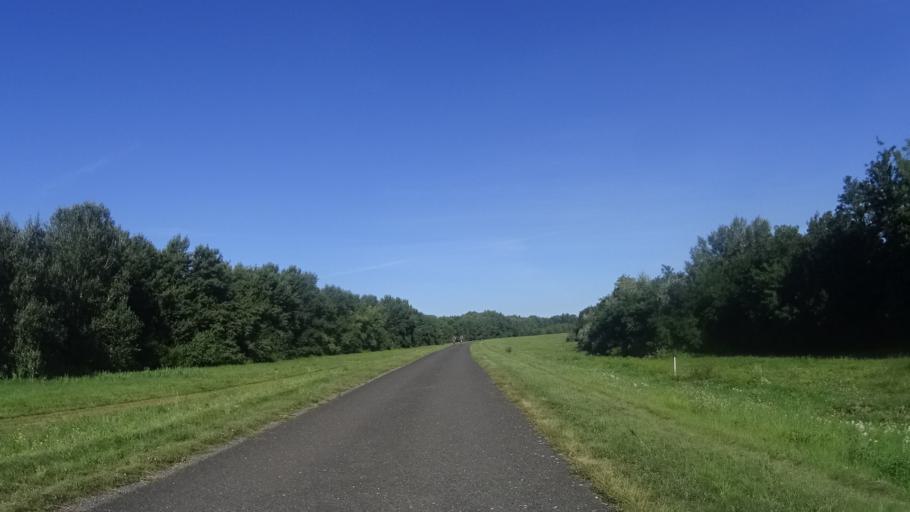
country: HU
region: Gyor-Moson-Sopron
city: Rajka
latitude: 48.0639
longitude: 17.1792
